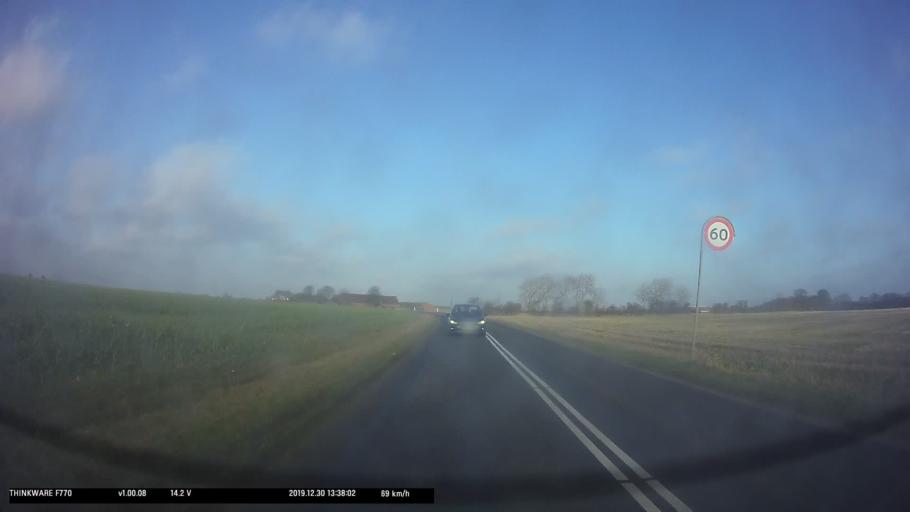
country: DK
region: South Denmark
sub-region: Fredericia Kommune
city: Fredericia
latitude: 55.5994
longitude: 9.7709
